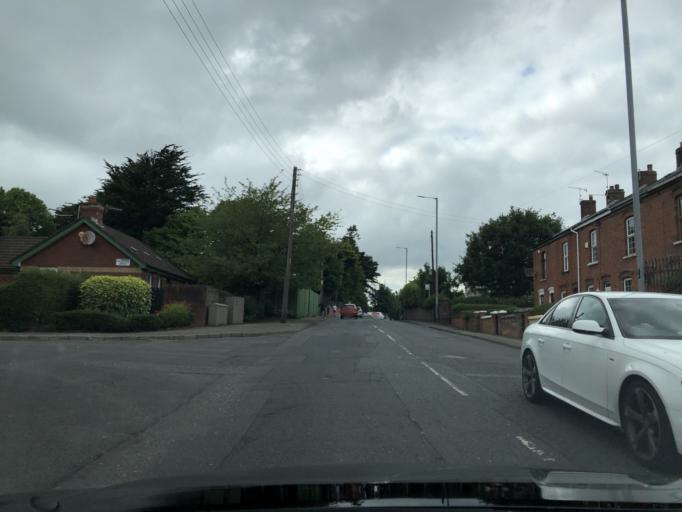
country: GB
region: Northern Ireland
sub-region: Newtownabbey District
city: Newtownabbey
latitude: 54.6536
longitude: -5.9217
